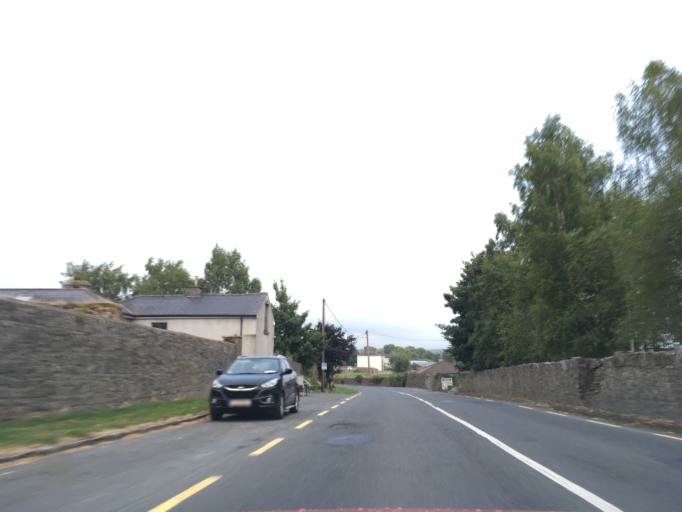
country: IE
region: Munster
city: Cashel
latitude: 52.4971
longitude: -7.9881
